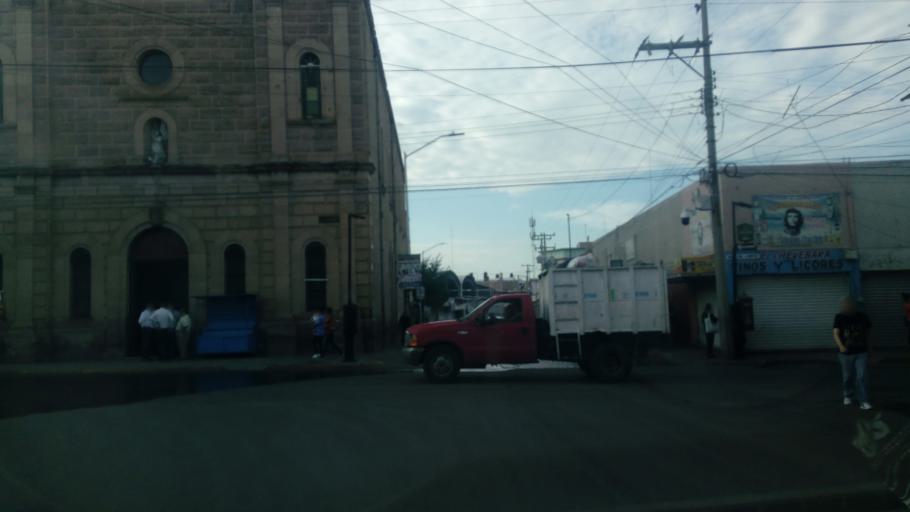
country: MX
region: Durango
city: Victoria de Durango
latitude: 24.0228
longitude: -104.6671
